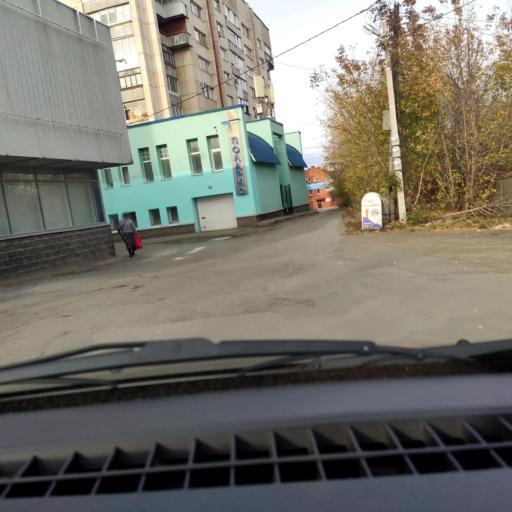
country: RU
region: Bashkortostan
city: Ufa
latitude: 54.7426
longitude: 55.9613
